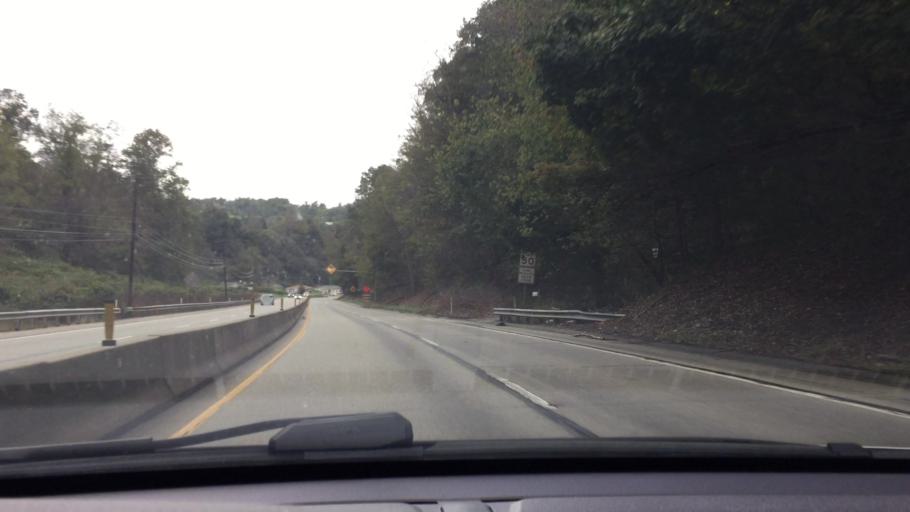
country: US
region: Pennsylvania
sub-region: Allegheny County
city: Elizabeth
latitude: 40.2463
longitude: -79.8737
